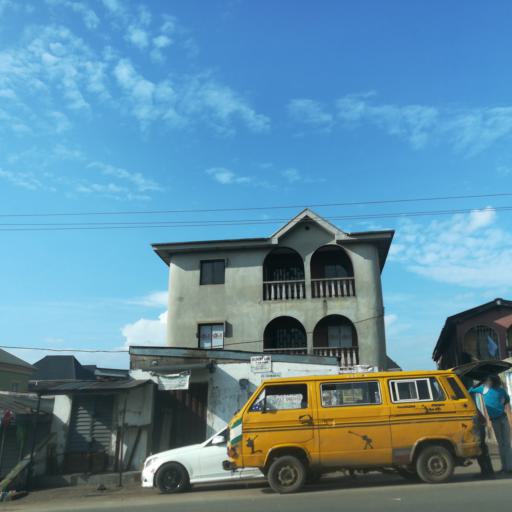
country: NG
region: Lagos
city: Agege
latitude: 6.6157
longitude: 3.3227
